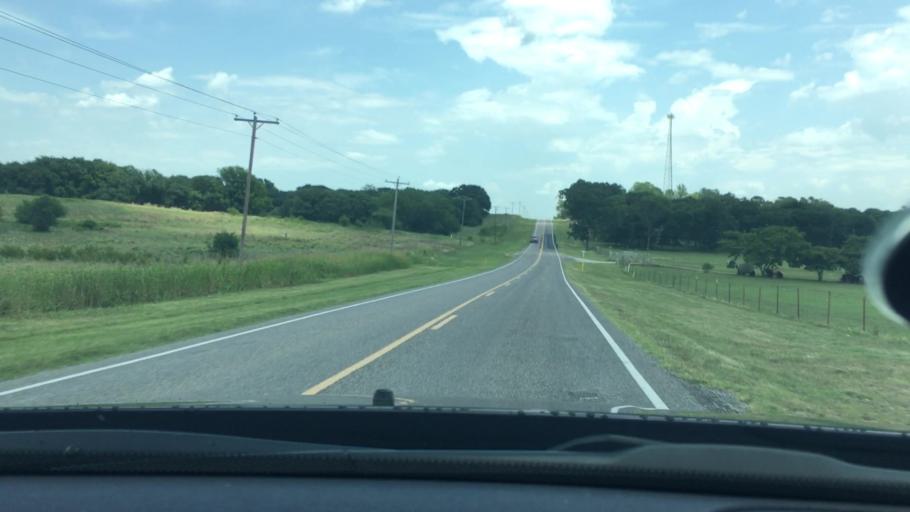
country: US
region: Oklahoma
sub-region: Carter County
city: Wilson
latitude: 33.9403
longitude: -97.3586
